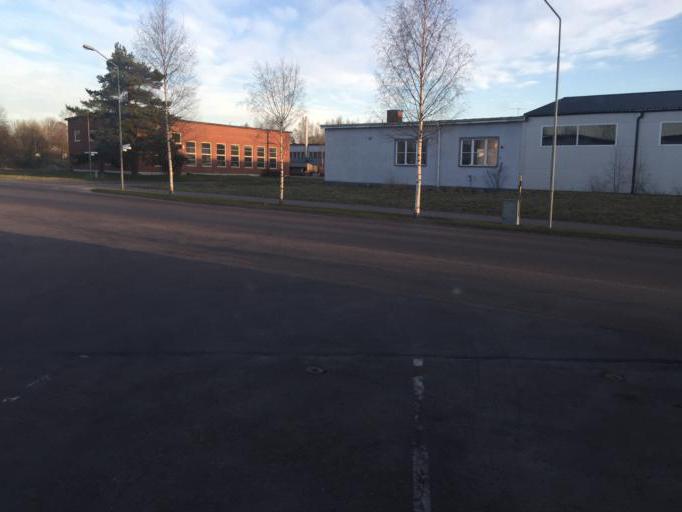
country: SE
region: Dalarna
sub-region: Borlange Kommun
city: Borlaenge
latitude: 60.4680
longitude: 15.4575
